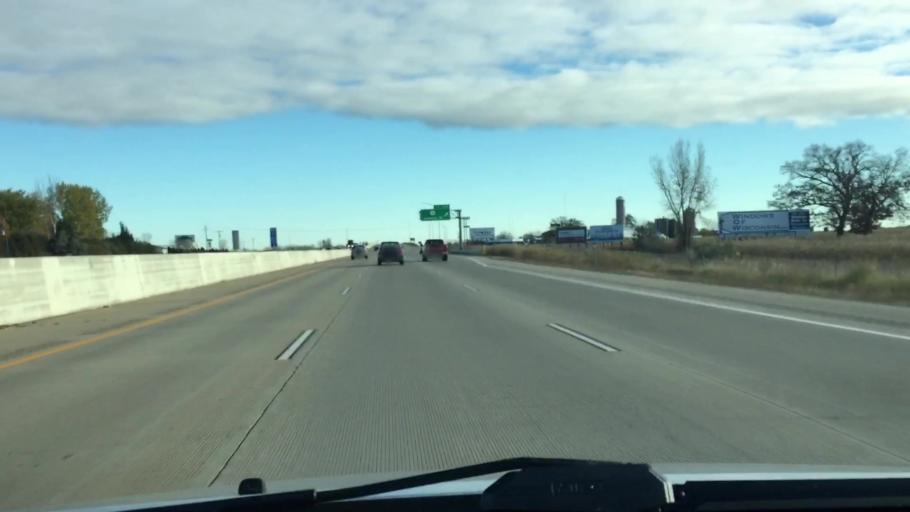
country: US
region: Wisconsin
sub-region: Winnebago County
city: Oshkosh
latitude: 44.0921
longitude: -88.5501
